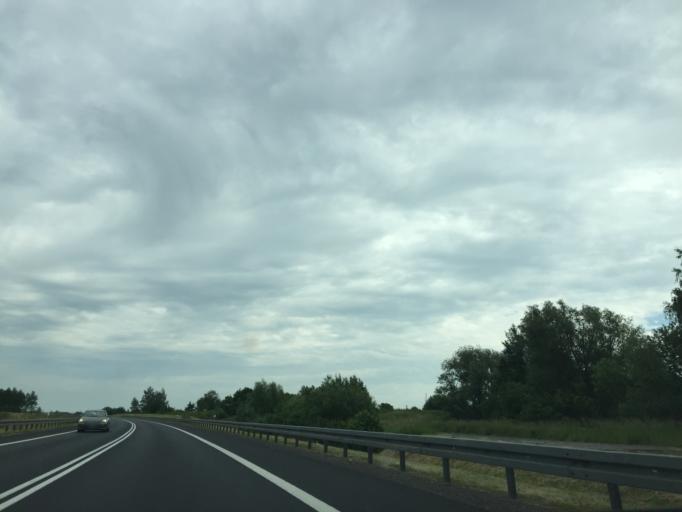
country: PL
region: Warmian-Masurian Voivodeship
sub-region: Powiat olsztynski
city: Biskupiec
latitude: 53.8336
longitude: 20.9183
